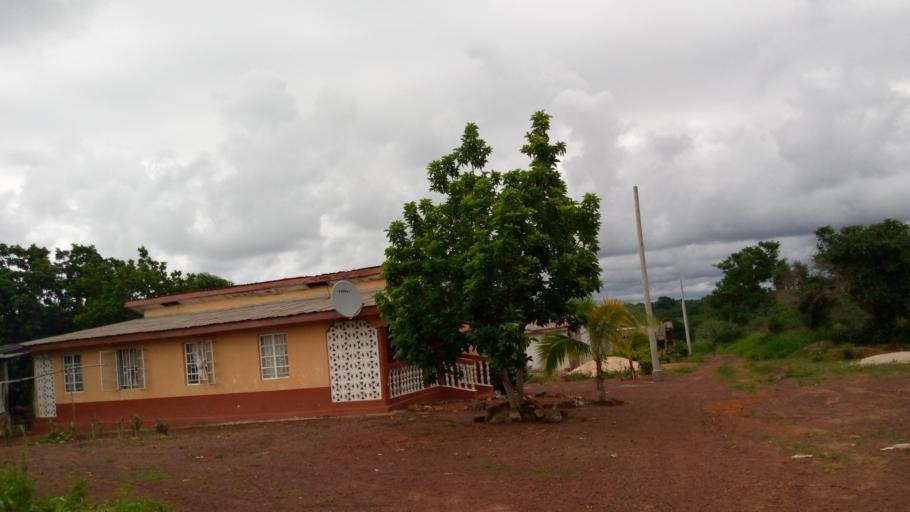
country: SL
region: Southern Province
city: Moyamba
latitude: 8.1648
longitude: -12.4468
